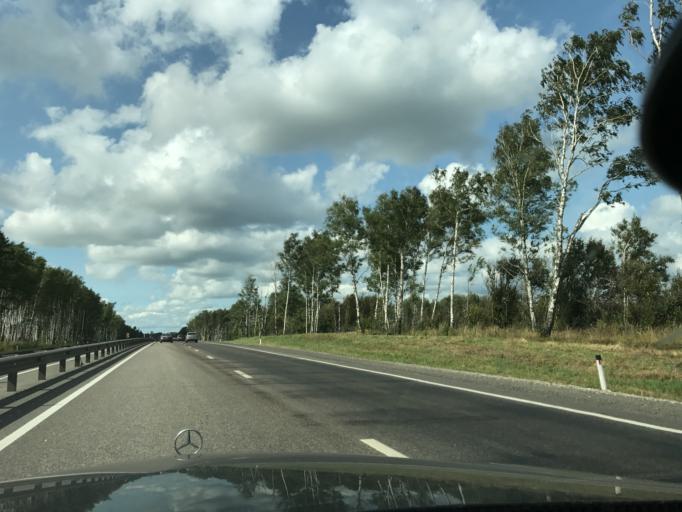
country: RU
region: Vladimir
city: Novovyazniki
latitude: 56.1958
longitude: 42.3727
